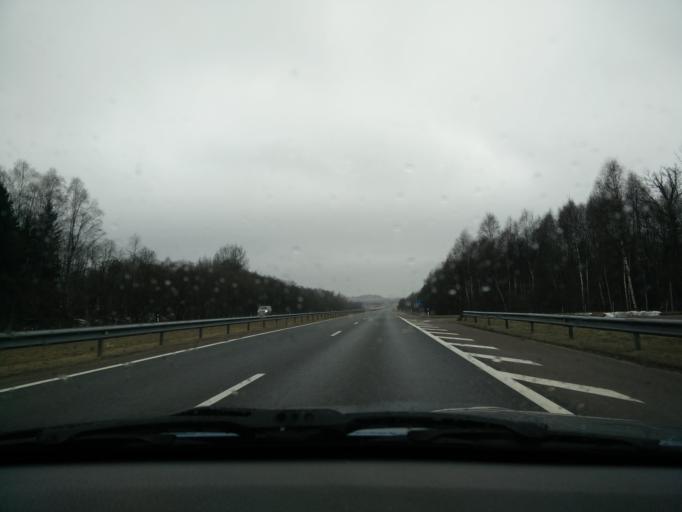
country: LT
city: Silale
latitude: 55.5741
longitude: 22.1671
